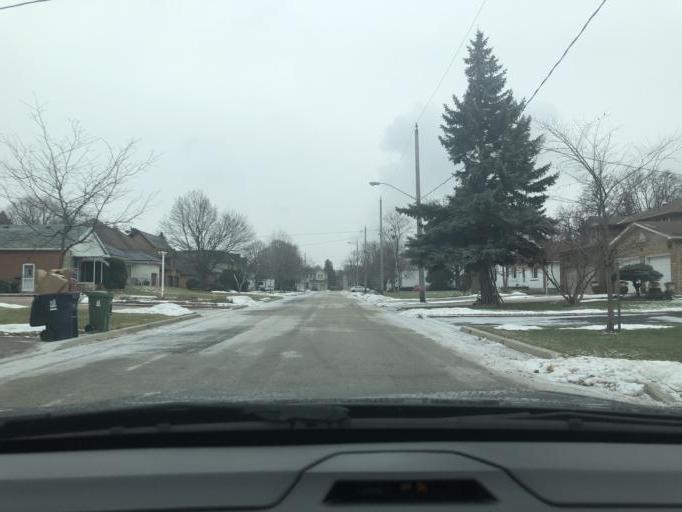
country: CA
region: Ontario
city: Scarborough
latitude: 43.7846
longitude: -79.2701
